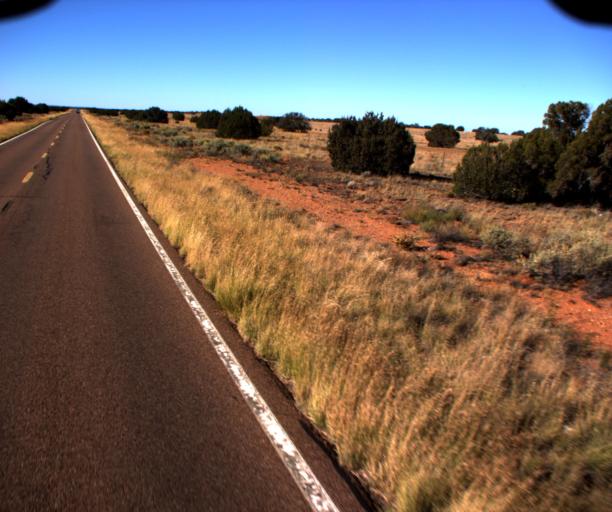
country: US
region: Arizona
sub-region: Navajo County
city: Heber-Overgaard
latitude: 34.5829
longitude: -110.4033
